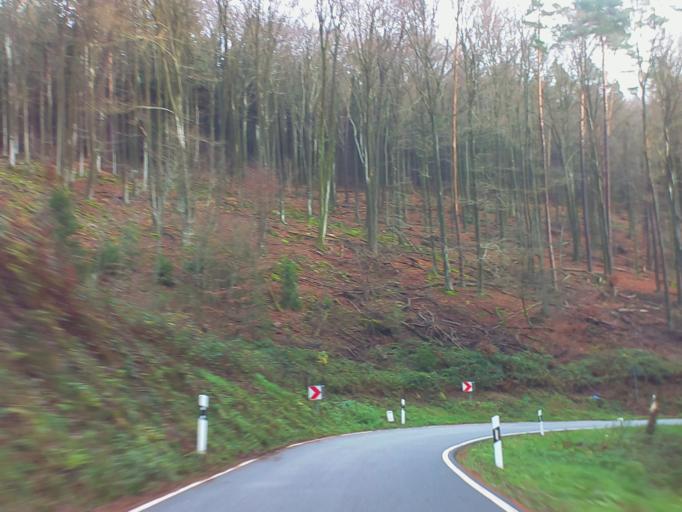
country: DE
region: Baden-Wuerttemberg
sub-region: Karlsruhe Region
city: Heddesbach
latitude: 49.4951
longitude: 8.8279
